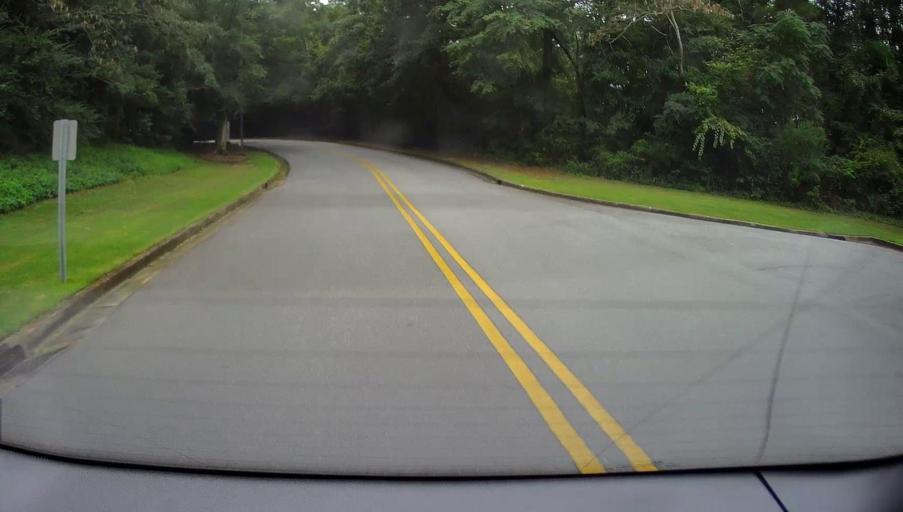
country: US
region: Georgia
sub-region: Bibb County
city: Macon
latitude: 32.8700
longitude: -83.6943
